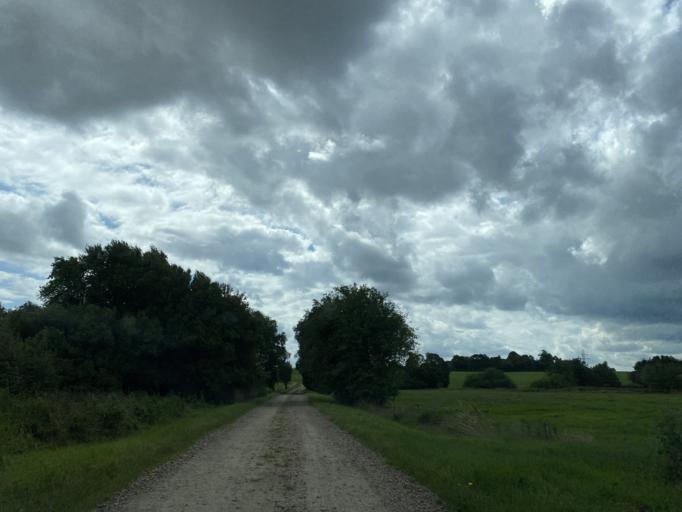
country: DK
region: Central Jutland
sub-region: Silkeborg Kommune
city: Silkeborg
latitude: 56.2171
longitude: 9.5704
